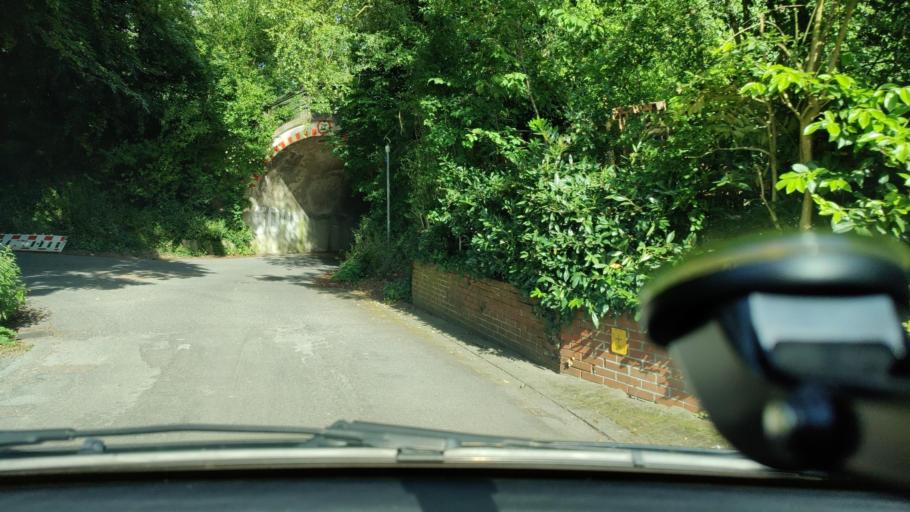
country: DE
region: North Rhine-Westphalia
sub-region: Regierungsbezirk Munster
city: Billerbeck
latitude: 52.0215
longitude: 7.2774
